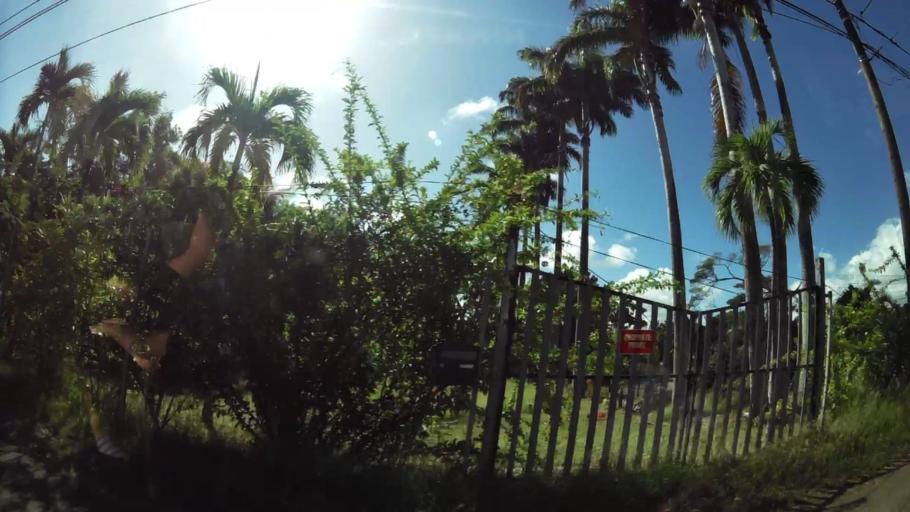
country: GP
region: Guadeloupe
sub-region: Guadeloupe
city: Sainte-Anne
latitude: 16.2308
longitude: -61.3768
